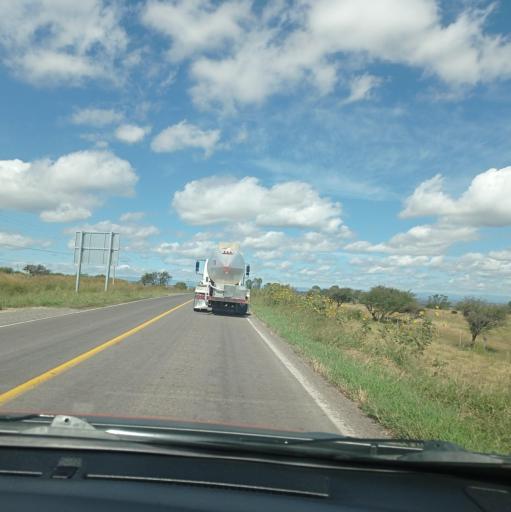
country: MX
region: Jalisco
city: Valle de Guadalupe
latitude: 21.0293
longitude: -102.5515
